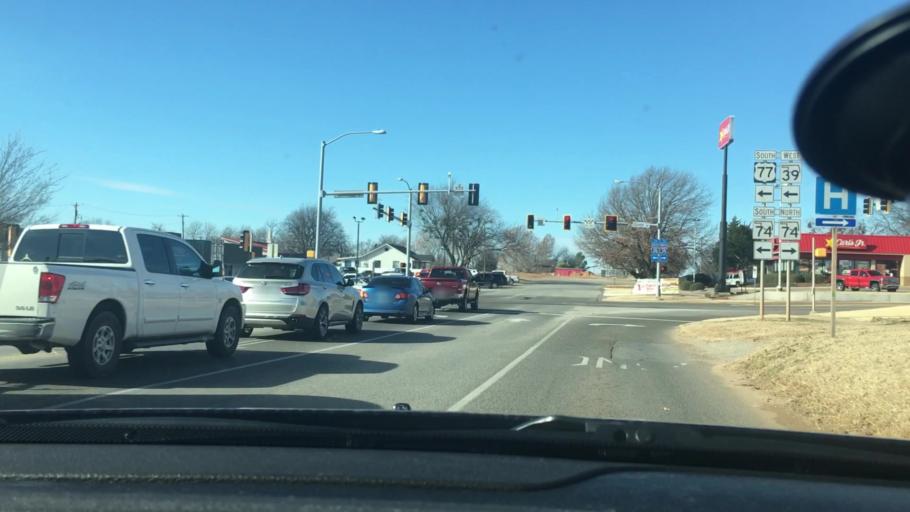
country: US
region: Oklahoma
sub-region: McClain County
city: Purcell
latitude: 35.0139
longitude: -97.3653
